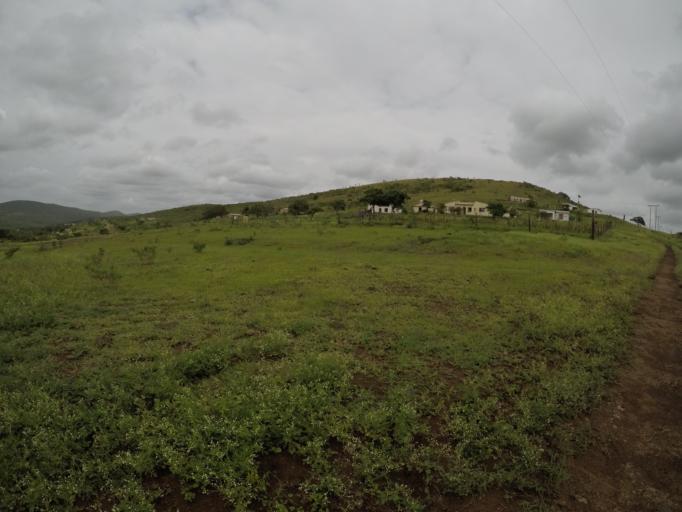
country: ZA
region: KwaZulu-Natal
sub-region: uThungulu District Municipality
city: Empangeni
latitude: -28.6175
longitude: 31.8923
